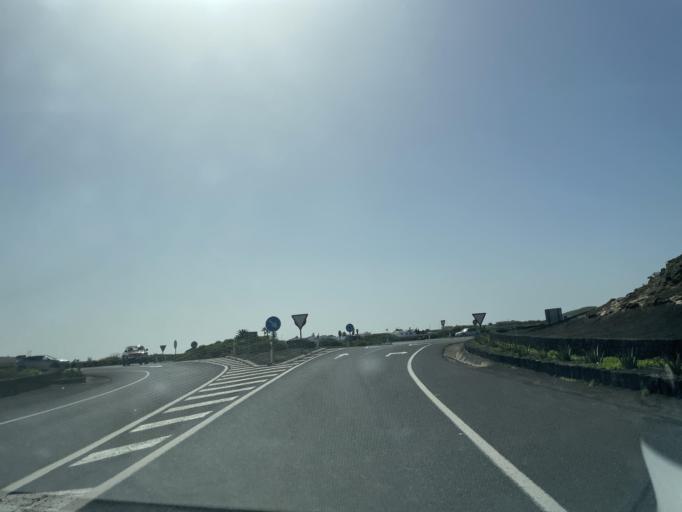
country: ES
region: Canary Islands
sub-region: Provincia de Las Palmas
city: San Bartolome
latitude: 29.0159
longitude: -13.6148
